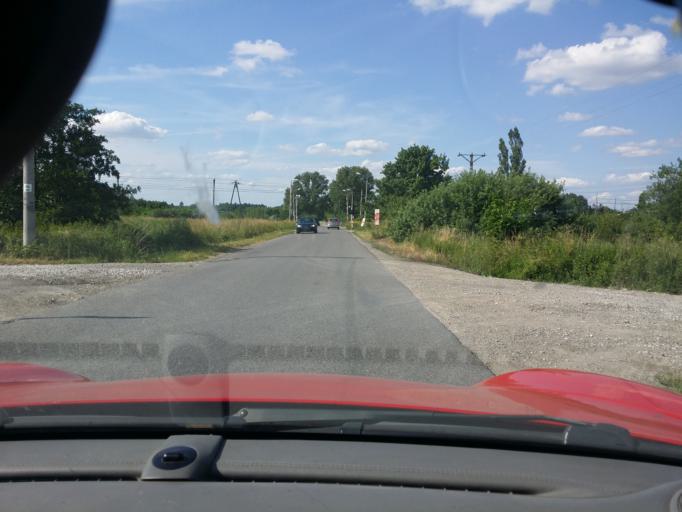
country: PL
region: Masovian Voivodeship
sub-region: Powiat radomski
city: Kowala
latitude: 51.3499
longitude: 21.0903
